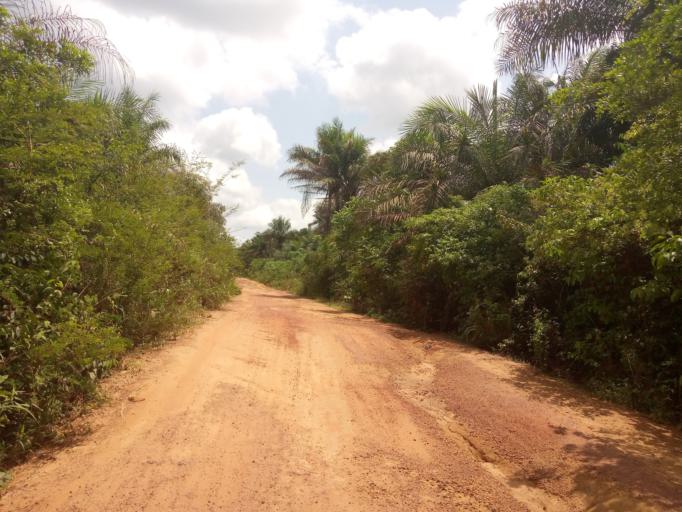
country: SL
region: Western Area
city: Waterloo
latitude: 8.3771
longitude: -12.9653
